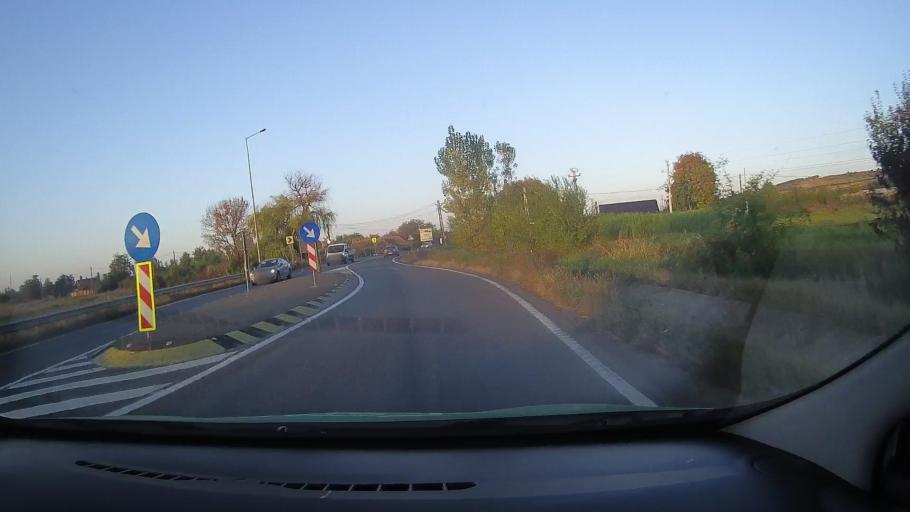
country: RO
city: Dioszeg
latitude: 47.2814
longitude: 21.9860
